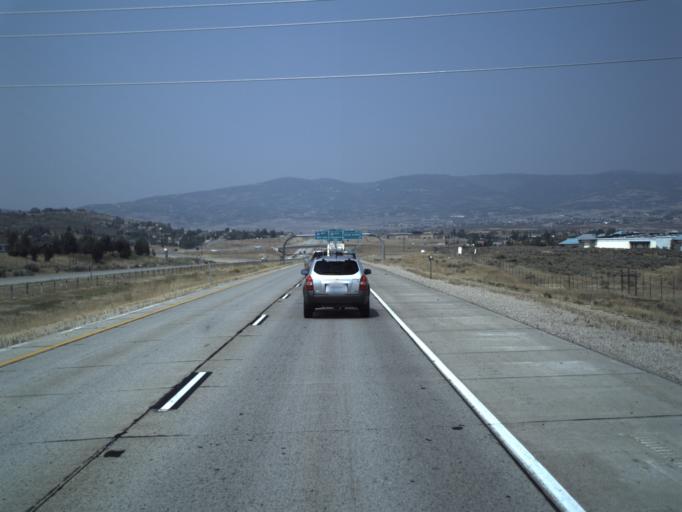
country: US
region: Utah
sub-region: Summit County
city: Snyderville
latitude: 40.7116
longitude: -111.4820
